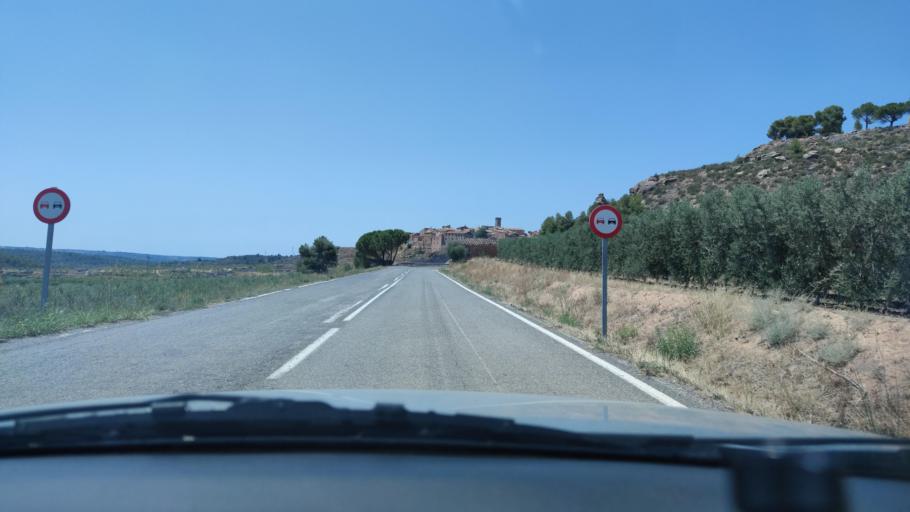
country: ES
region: Catalonia
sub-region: Provincia de Lleida
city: el Cogul
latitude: 41.4320
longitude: 0.6561
